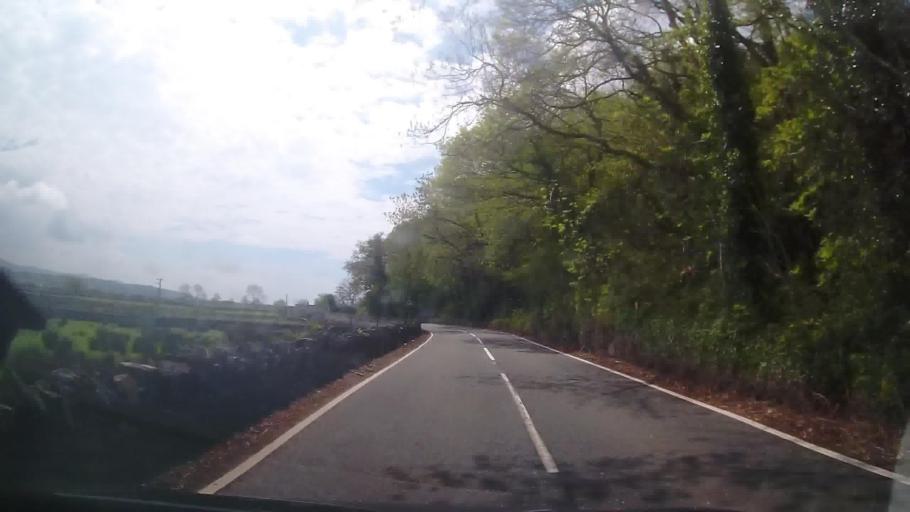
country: GB
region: Wales
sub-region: Gwynedd
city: Porthmadog
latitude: 52.9506
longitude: -4.1069
